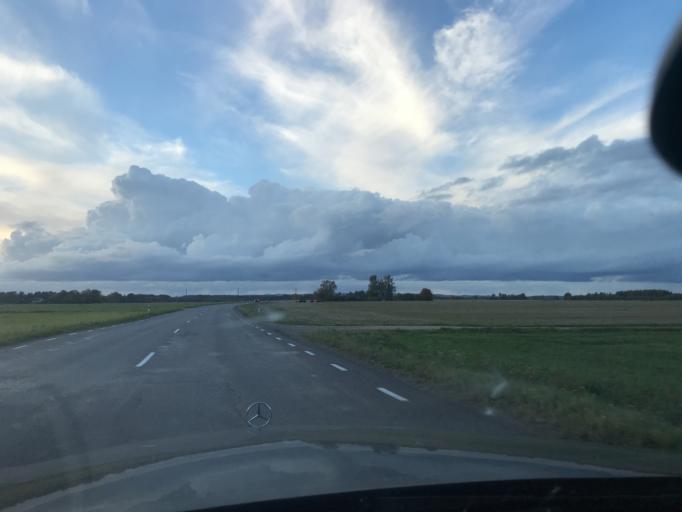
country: EE
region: Vorumaa
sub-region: Antsla vald
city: Vana-Antsla
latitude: 57.8971
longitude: 26.4840
